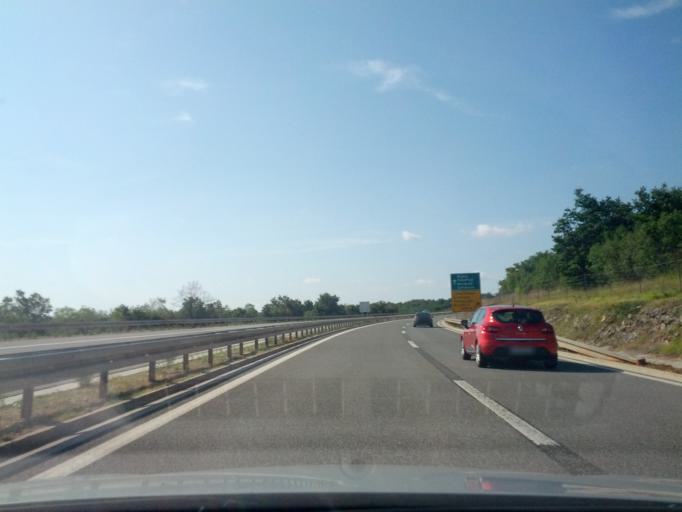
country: HR
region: Istarska
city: Buje
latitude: 45.4137
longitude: 13.6215
